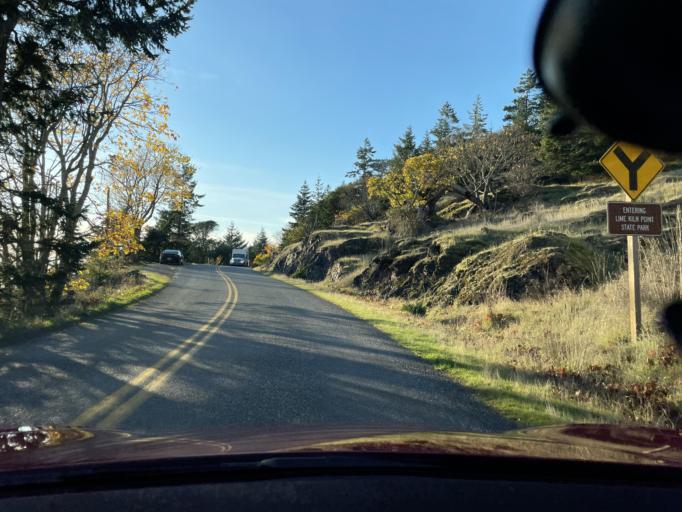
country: US
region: Washington
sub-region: San Juan County
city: Friday Harbor
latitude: 48.5140
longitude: -123.1469
